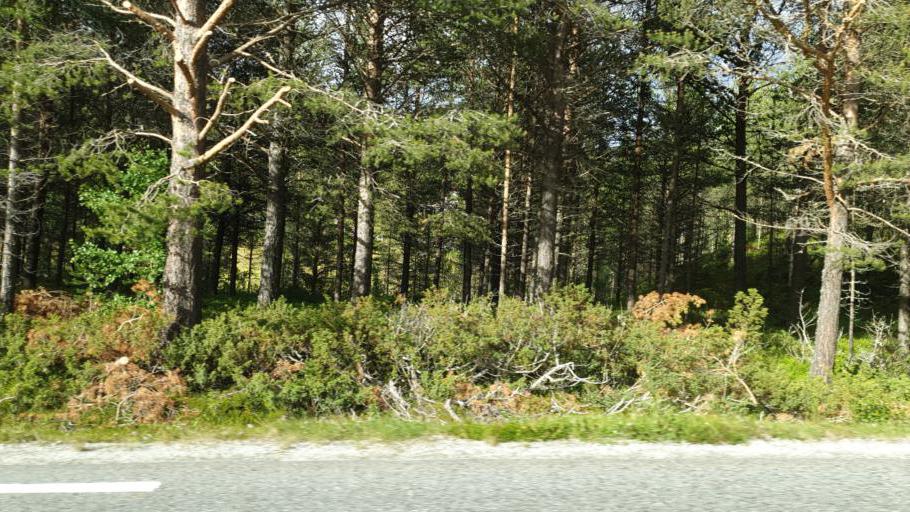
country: NO
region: Oppland
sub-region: Vaga
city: Vagamo
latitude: 61.8242
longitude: 8.9714
